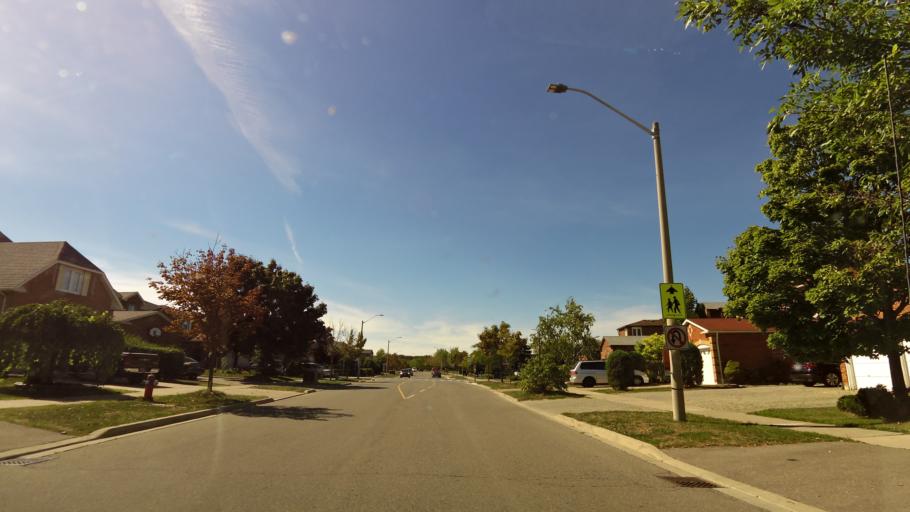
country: CA
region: Ontario
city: Mississauga
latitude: 43.6047
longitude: -79.6617
